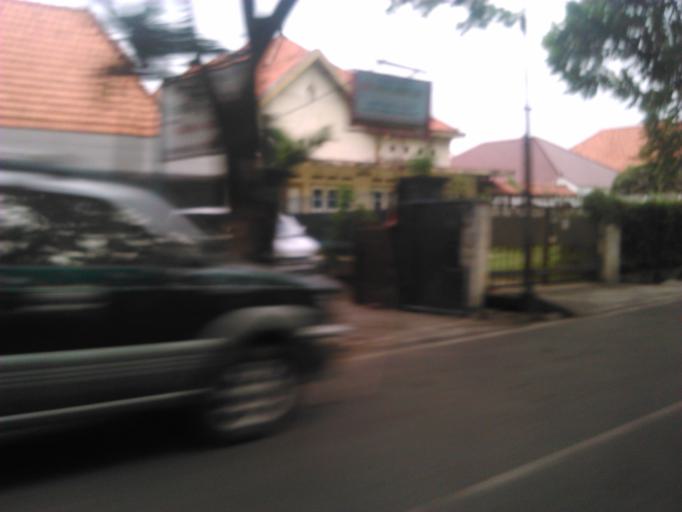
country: ID
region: East Java
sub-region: Kota Surabaya
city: Surabaya
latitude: -7.2607
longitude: 112.7270
